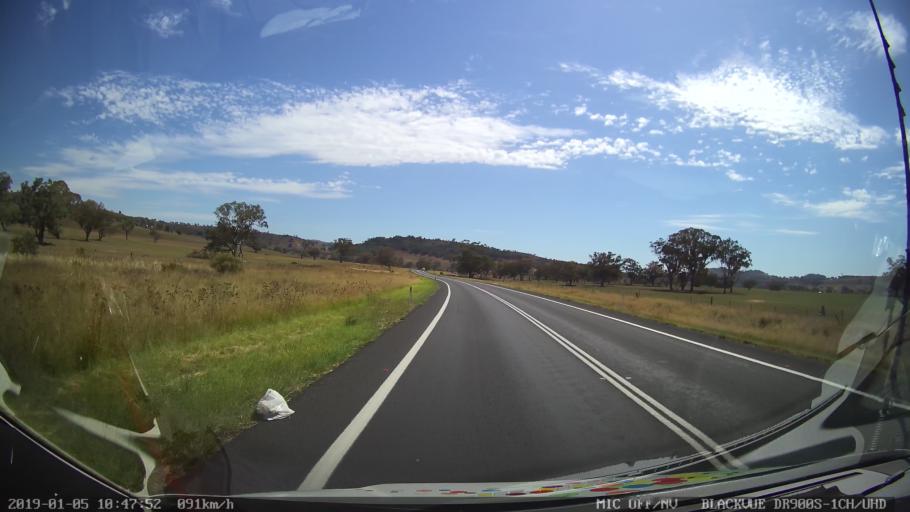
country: AU
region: New South Wales
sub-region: Warrumbungle Shire
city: Coonabarabran
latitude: -31.4414
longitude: 149.0386
